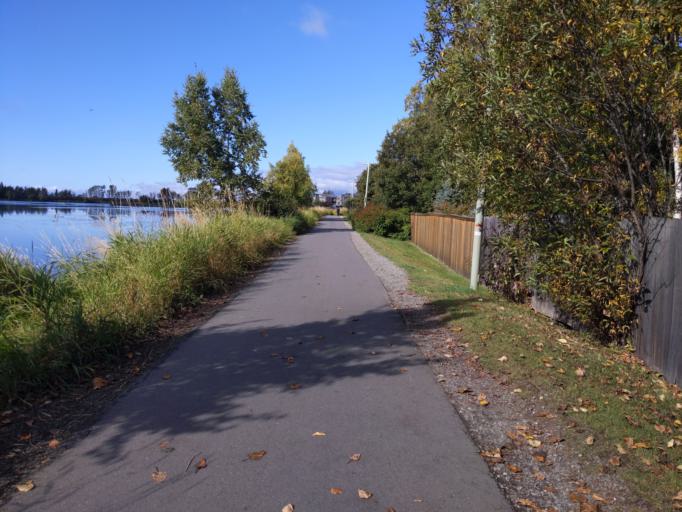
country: US
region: Alaska
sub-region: Anchorage Municipality
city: Anchorage
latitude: 61.2062
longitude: -149.9142
